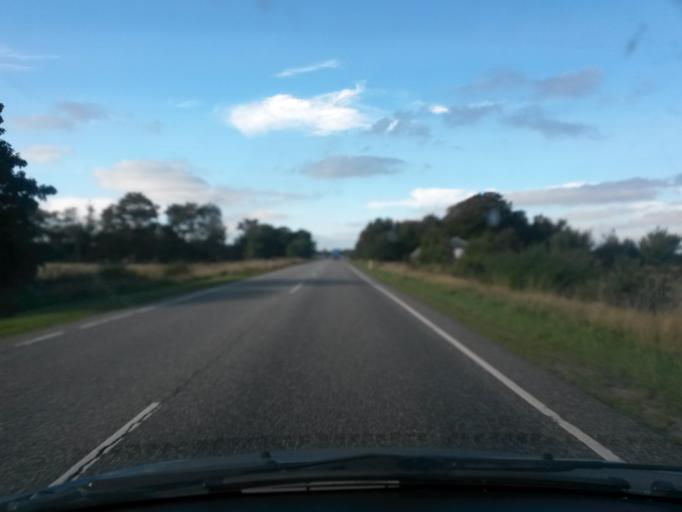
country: DK
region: Central Jutland
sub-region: Holstebro Kommune
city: Holstebro
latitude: 56.3247
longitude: 8.6687
